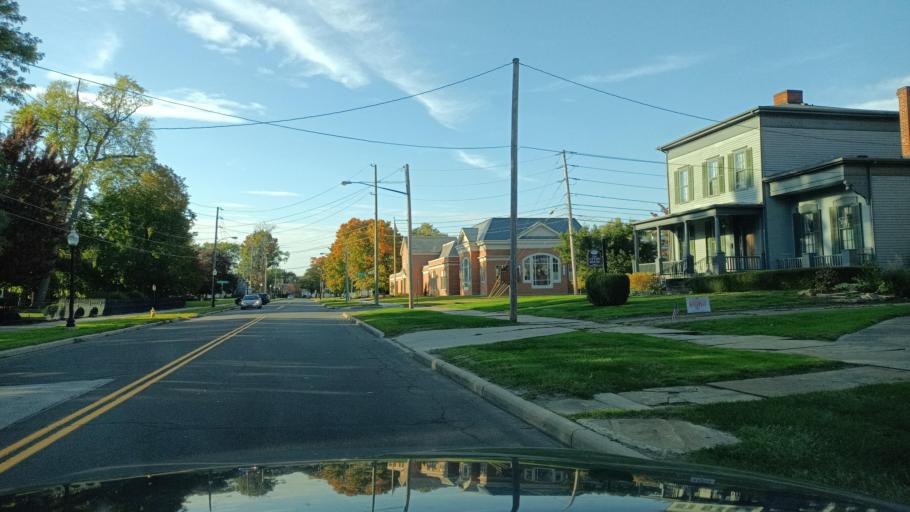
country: CN
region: Xinjiang Uygur Zizhiqu
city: Jiamu
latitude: 41.2391
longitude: 80.8222
